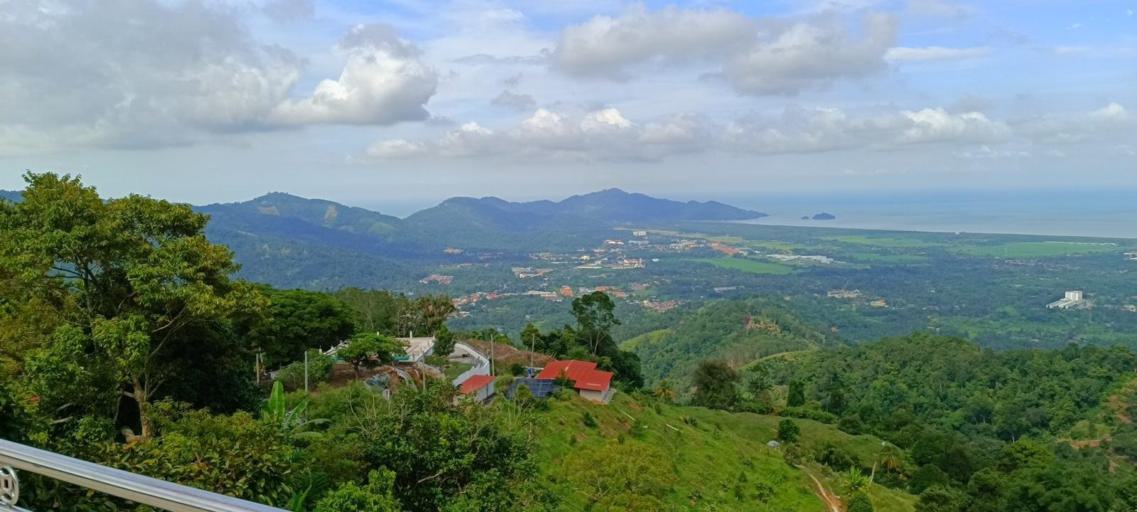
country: MY
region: Penang
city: Kampung Sungai Ara
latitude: 5.3766
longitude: 100.2438
